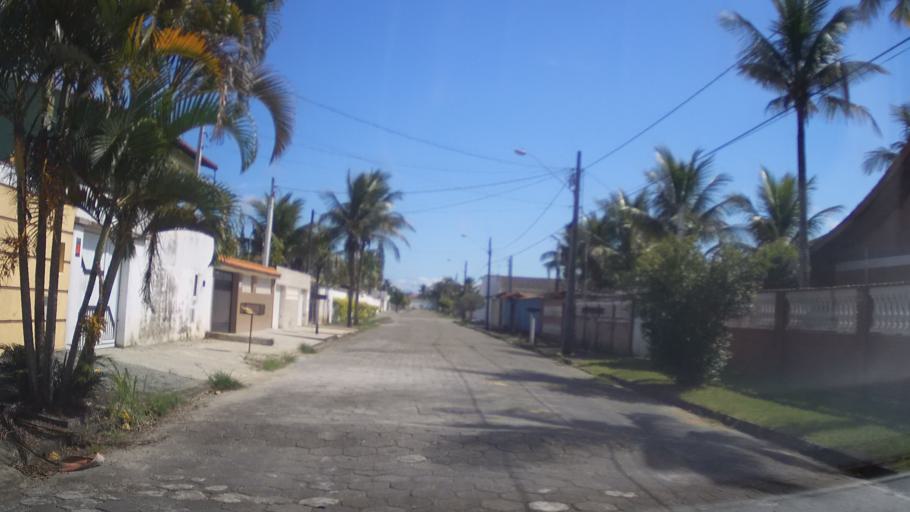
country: BR
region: Sao Paulo
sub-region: Itanhaem
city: Itanhaem
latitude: -24.1532
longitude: -46.7290
